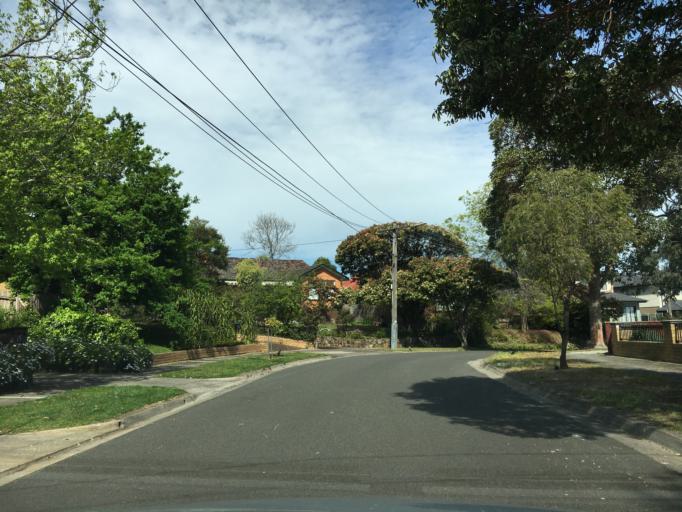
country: AU
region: Victoria
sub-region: Monash
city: Chadstone
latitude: -37.8897
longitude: 145.1141
